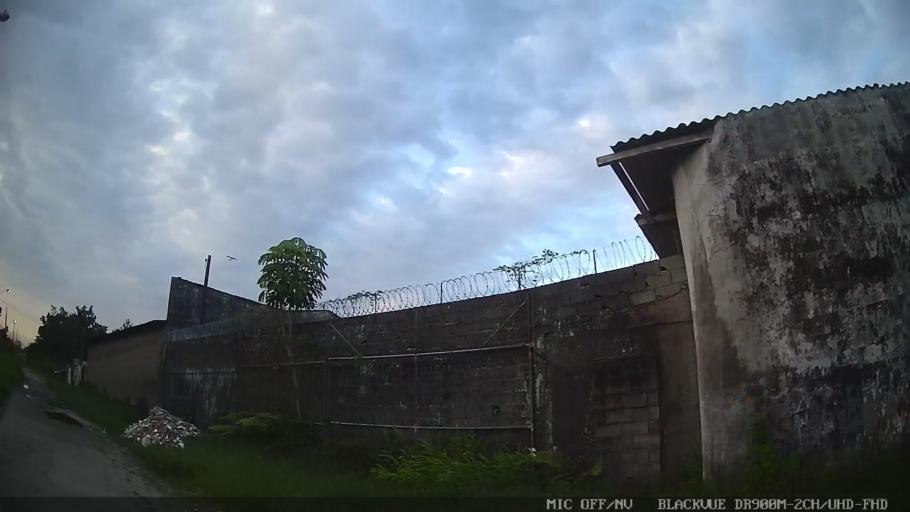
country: BR
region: Sao Paulo
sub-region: Itanhaem
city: Itanhaem
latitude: -24.1716
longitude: -46.7769
